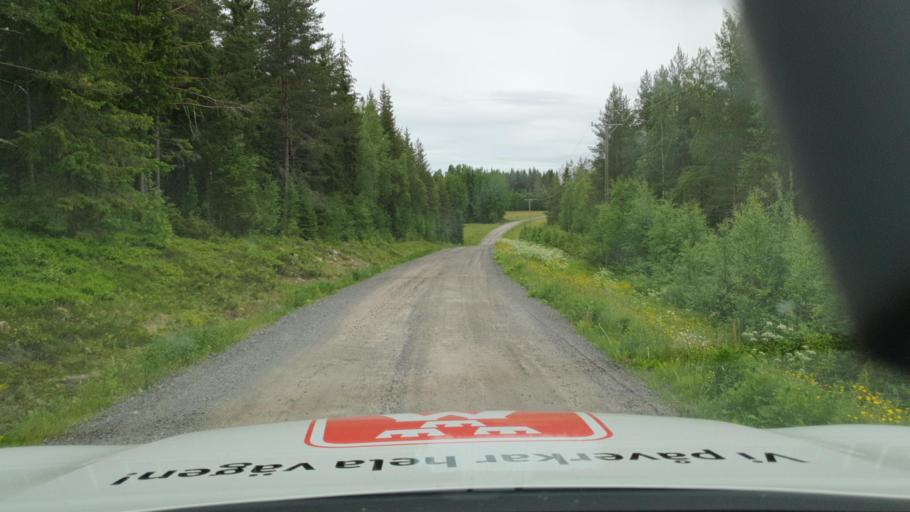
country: SE
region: Vaesterbotten
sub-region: Skelleftea Kommun
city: Burtraesk
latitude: 64.3593
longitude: 20.6159
